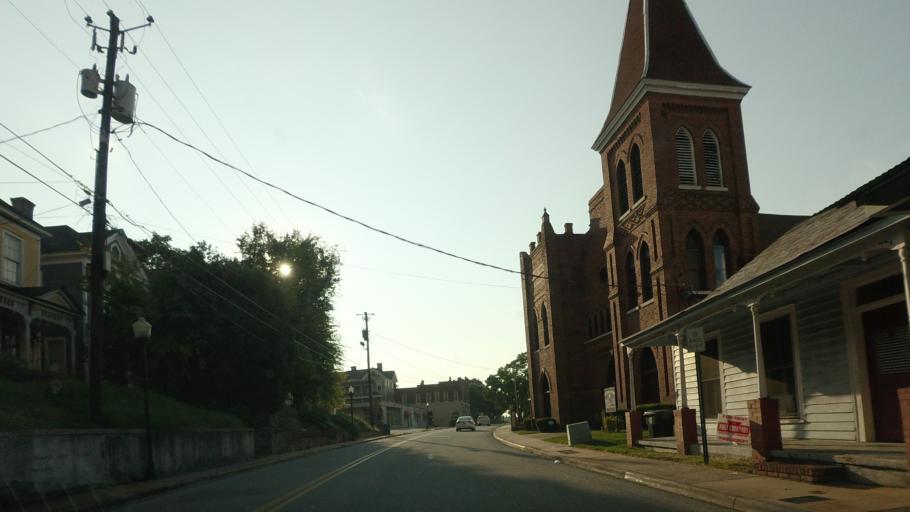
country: US
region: Georgia
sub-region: Bibb County
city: Macon
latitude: 32.8383
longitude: -83.6364
